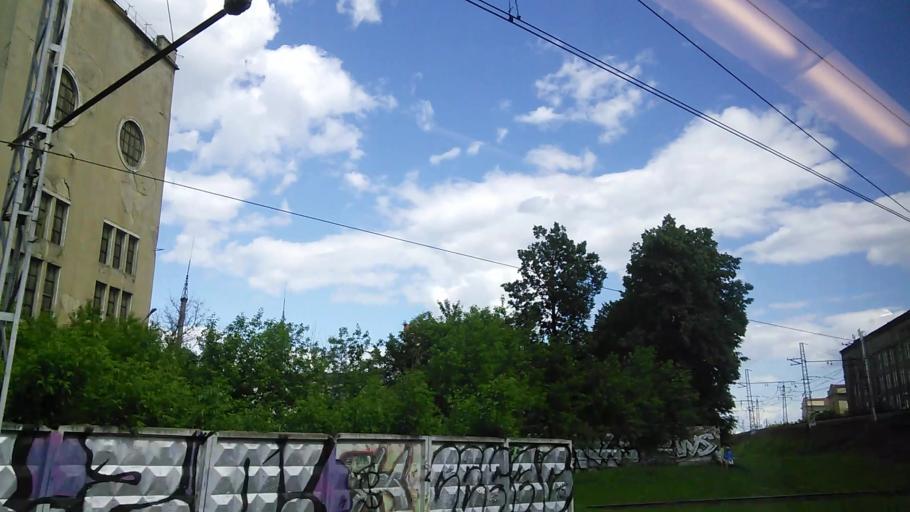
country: RU
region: Moscow
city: Mar'ina Roshcha
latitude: 55.8092
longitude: 37.5839
